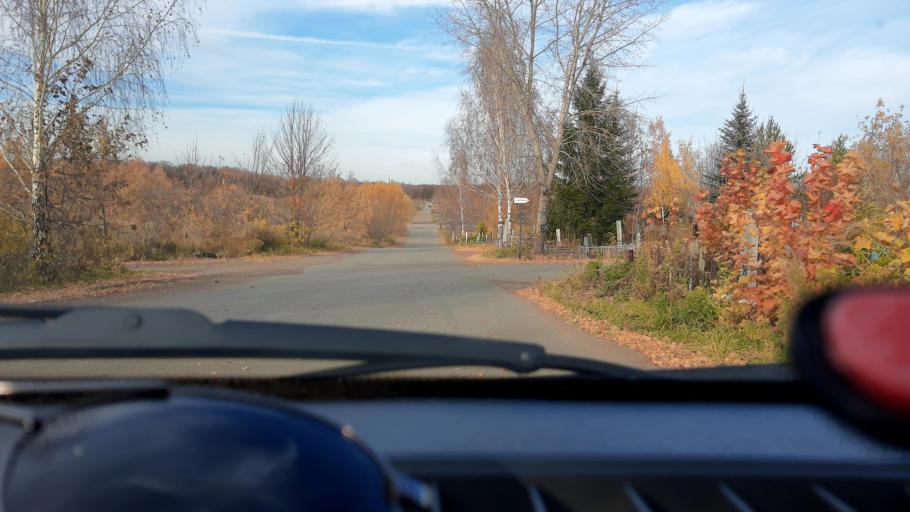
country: RU
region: Bashkortostan
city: Ufa
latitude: 54.8578
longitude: 56.1569
